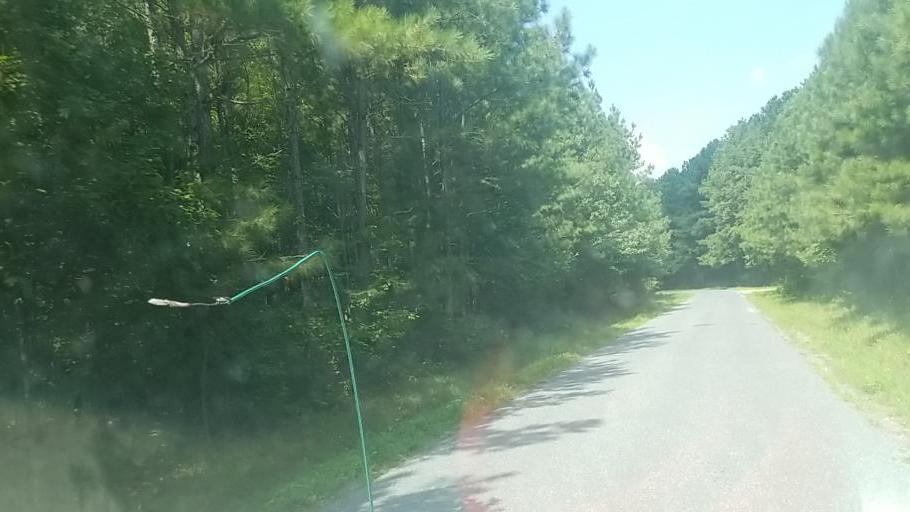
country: US
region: Maryland
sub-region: Worcester County
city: Berlin
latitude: 38.2870
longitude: -75.3087
